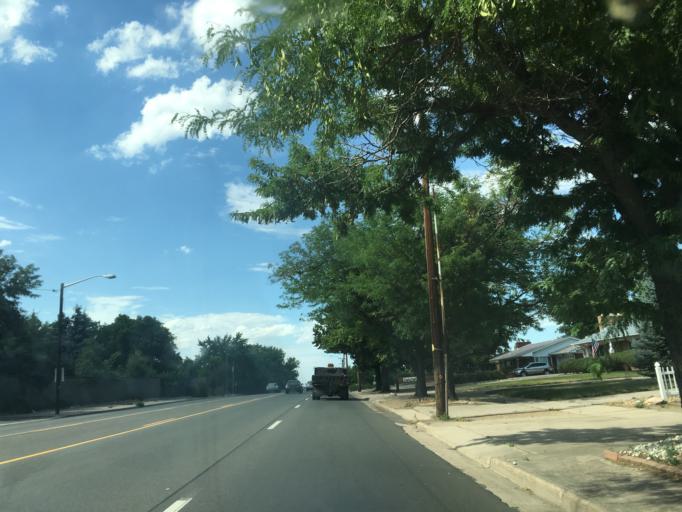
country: US
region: Colorado
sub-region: Arapahoe County
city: Sheridan
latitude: 39.6711
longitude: -105.0532
